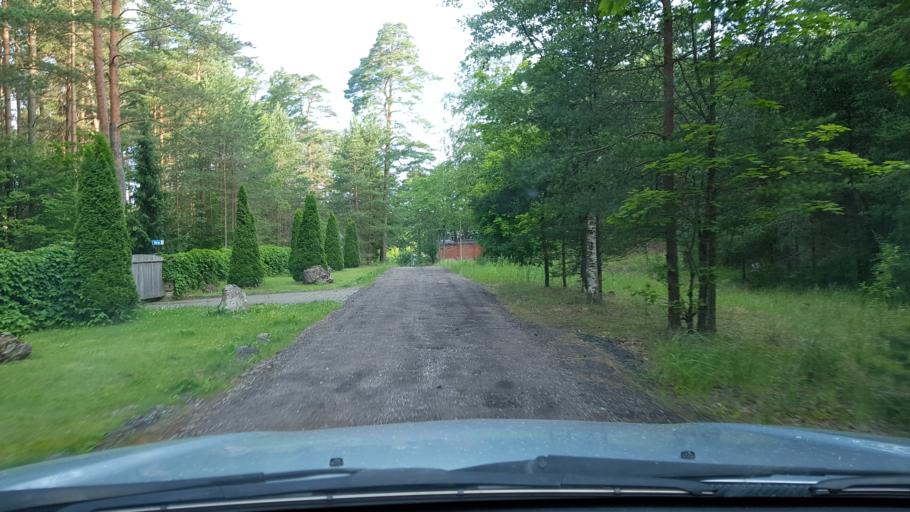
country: EE
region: Ida-Virumaa
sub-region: Narva-Joesuu linn
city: Narva-Joesuu
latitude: 59.4538
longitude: 28.0389
